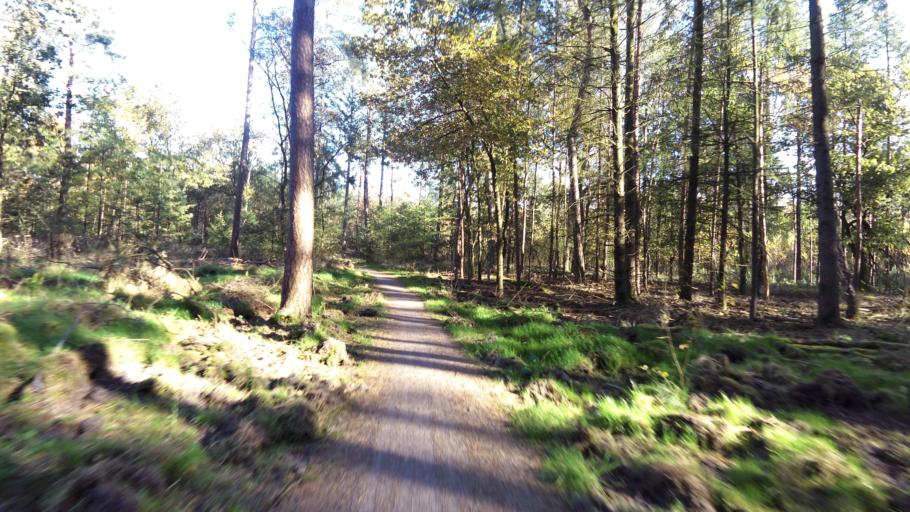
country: NL
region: Gelderland
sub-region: Gemeente Epe
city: Epe
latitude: 52.3679
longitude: 5.9635
